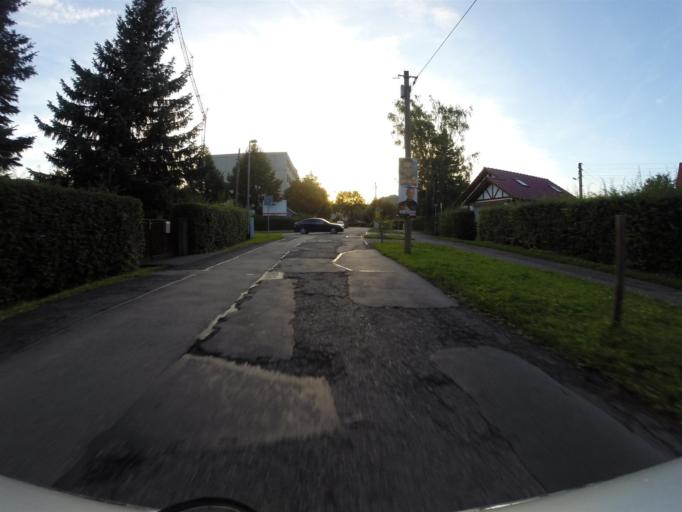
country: DE
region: Thuringia
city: Jena
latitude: 50.9048
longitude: 11.5749
